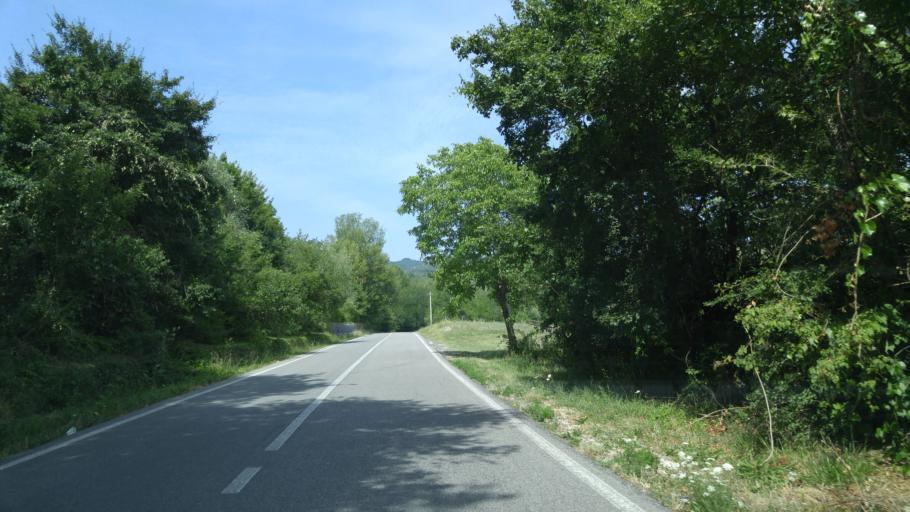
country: IT
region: The Marches
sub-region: Provincia di Pesaro e Urbino
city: Cantiano
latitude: 43.4838
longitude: 12.6186
